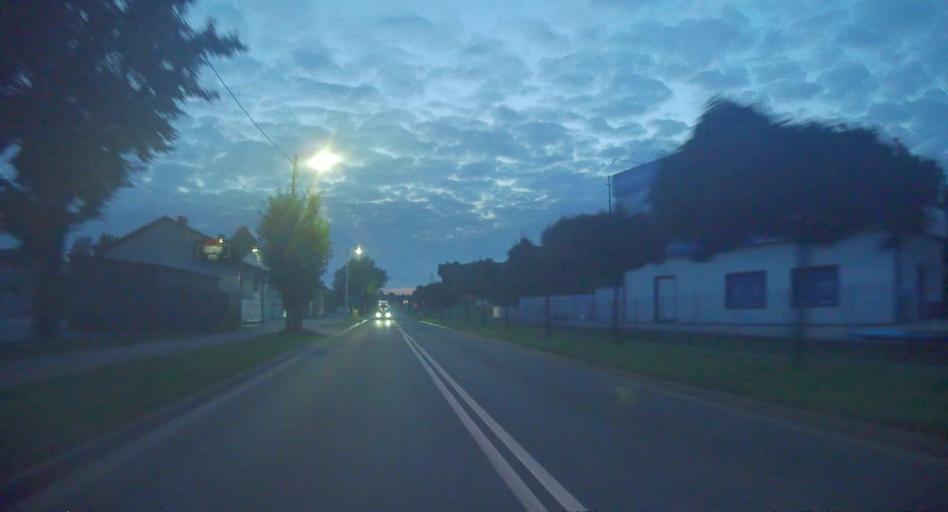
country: PL
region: Silesian Voivodeship
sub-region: Powiat klobucki
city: Klobuck
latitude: 50.9044
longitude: 18.9259
